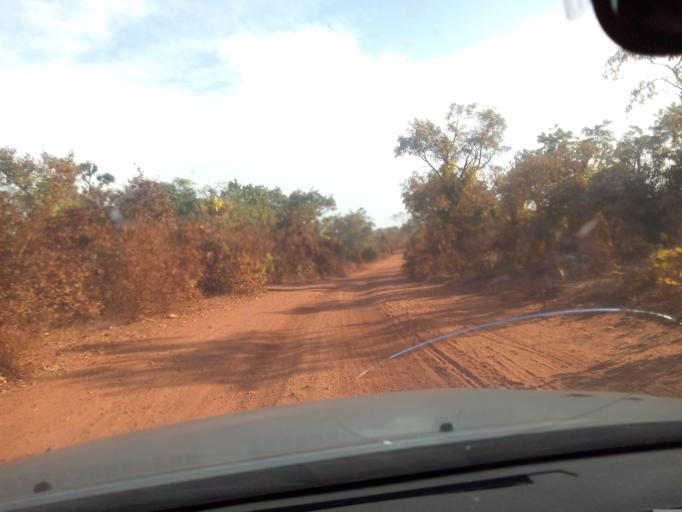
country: ML
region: Sikasso
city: Sikasso
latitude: 11.4334
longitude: -5.5570
